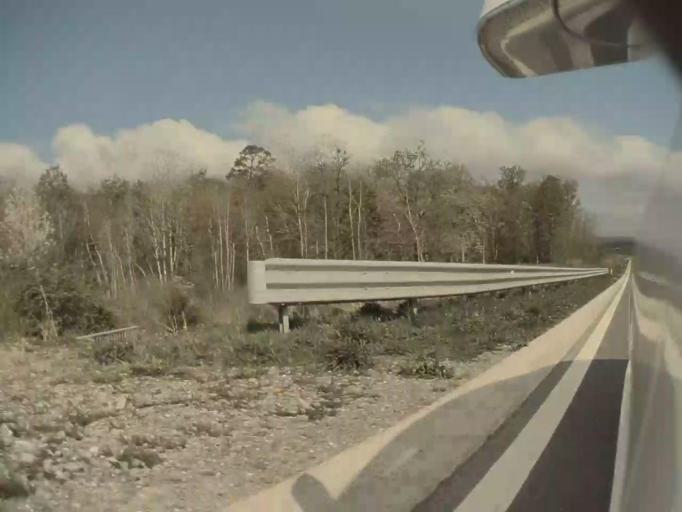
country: BE
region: Wallonia
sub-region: Province du Luxembourg
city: Marche-en-Famenne
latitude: 50.2188
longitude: 5.3159
